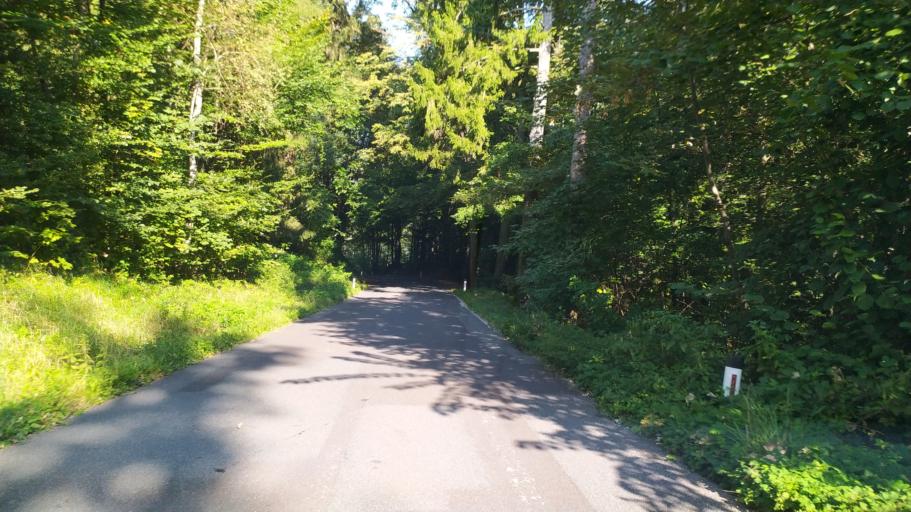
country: AT
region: Lower Austria
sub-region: Politischer Bezirk Amstetten
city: Zeillern
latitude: 48.1535
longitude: 14.7464
